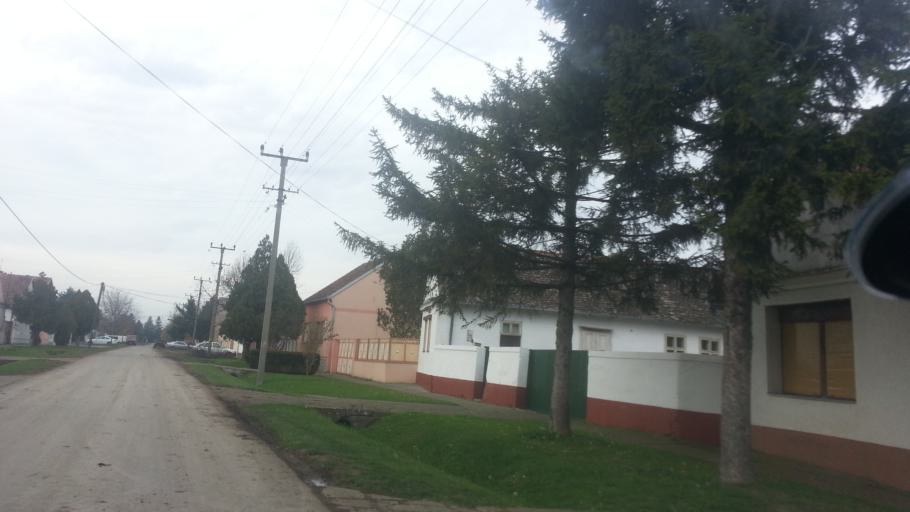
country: RS
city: Putinci
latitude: 44.9639
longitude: 19.9796
